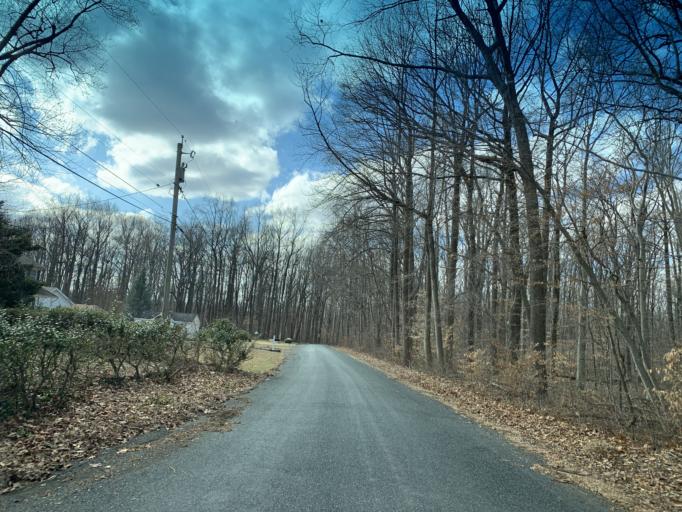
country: US
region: Maryland
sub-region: Harford County
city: Riverside
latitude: 39.5099
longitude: -76.2402
